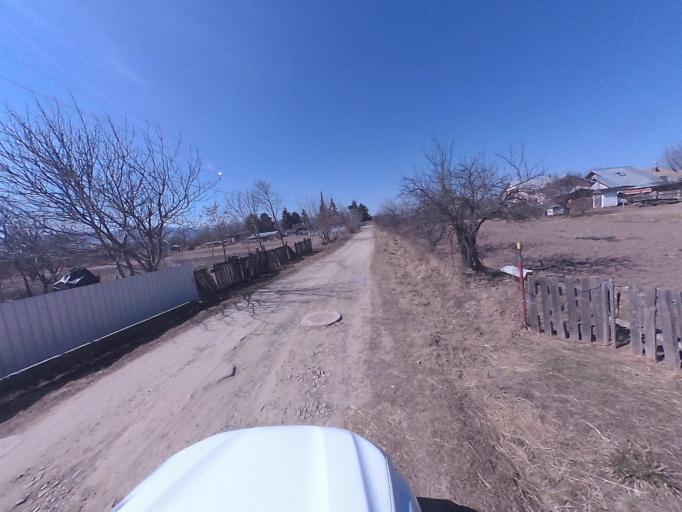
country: RO
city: Vanatori-Neamt
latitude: 47.1824
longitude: 26.3297
